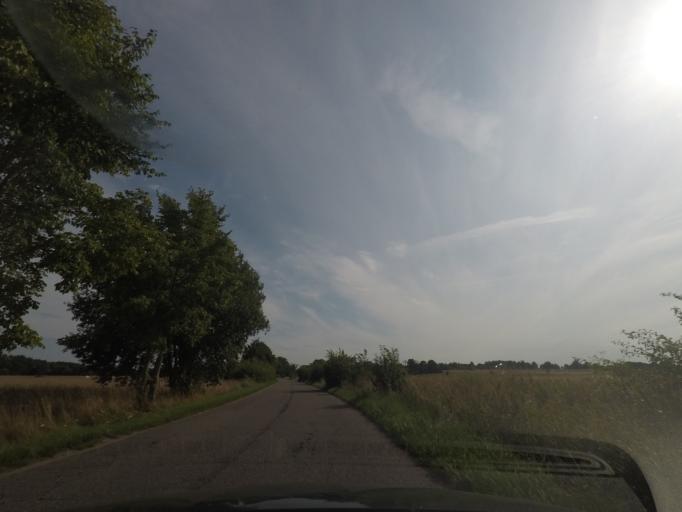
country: PL
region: Pomeranian Voivodeship
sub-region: Powiat slupski
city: Smoldzino
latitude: 54.6229
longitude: 17.2410
